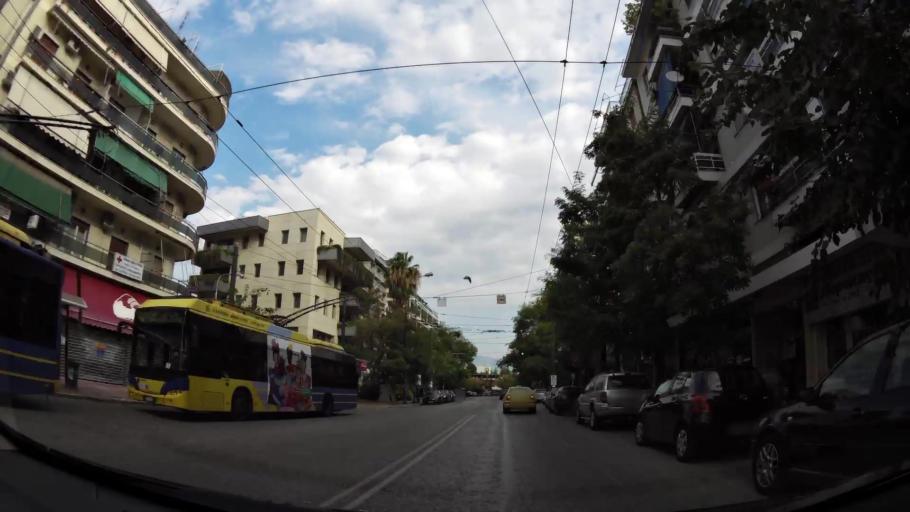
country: GR
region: Attica
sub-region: Nomarchia Athinas
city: Nea Chalkidona
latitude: 38.0218
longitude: 23.7357
